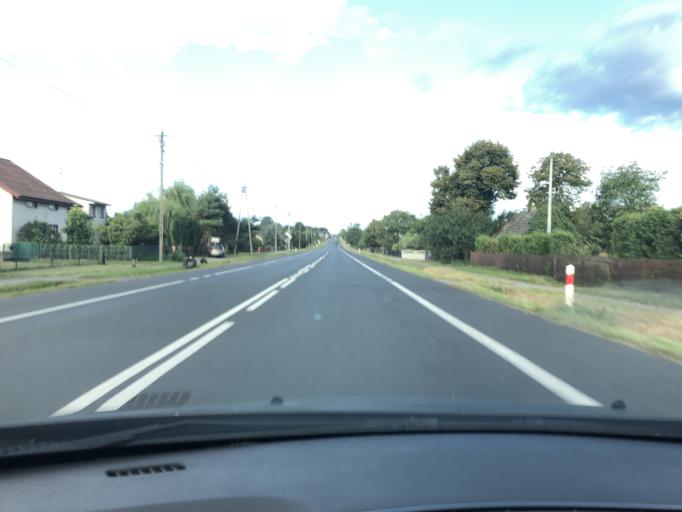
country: PL
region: Lodz Voivodeship
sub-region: Powiat wieruszowski
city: Sokolniki
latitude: 51.3050
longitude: 18.3113
